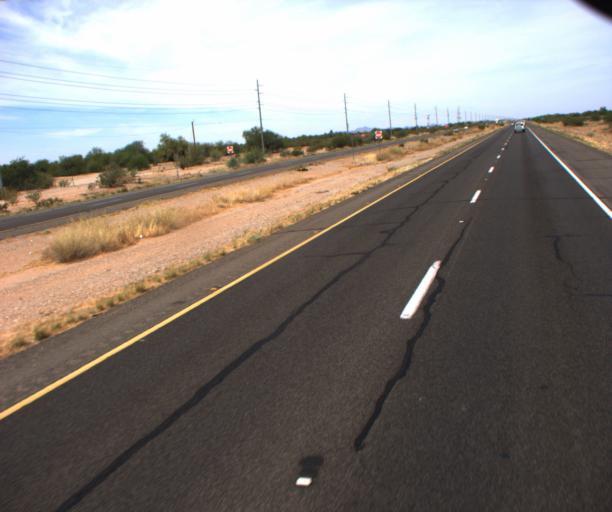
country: US
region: Arizona
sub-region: Maricopa County
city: Sun City West
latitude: 33.7221
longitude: -112.4569
